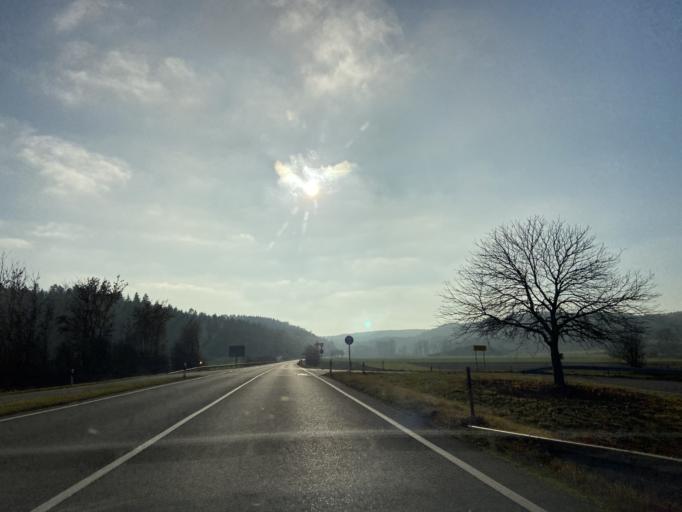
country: DE
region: Baden-Wuerttemberg
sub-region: Tuebingen Region
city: Veringenstadt
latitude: 48.1736
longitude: 9.2080
